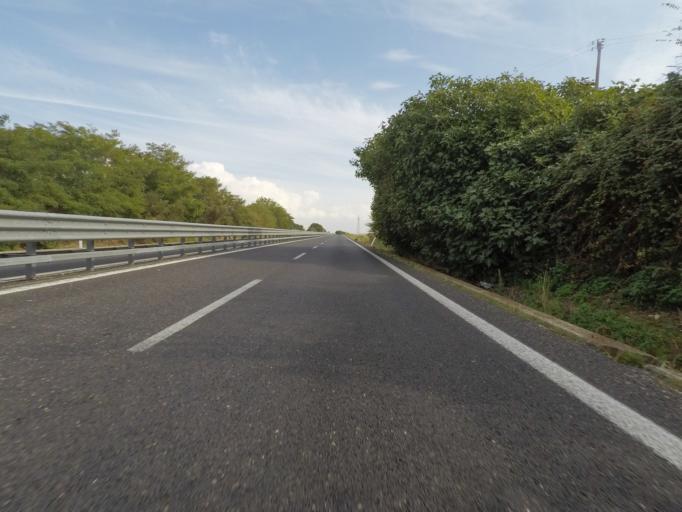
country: IT
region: Latium
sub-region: Provincia di Viterbo
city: Pescia Romana
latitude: 42.3928
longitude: 11.5330
